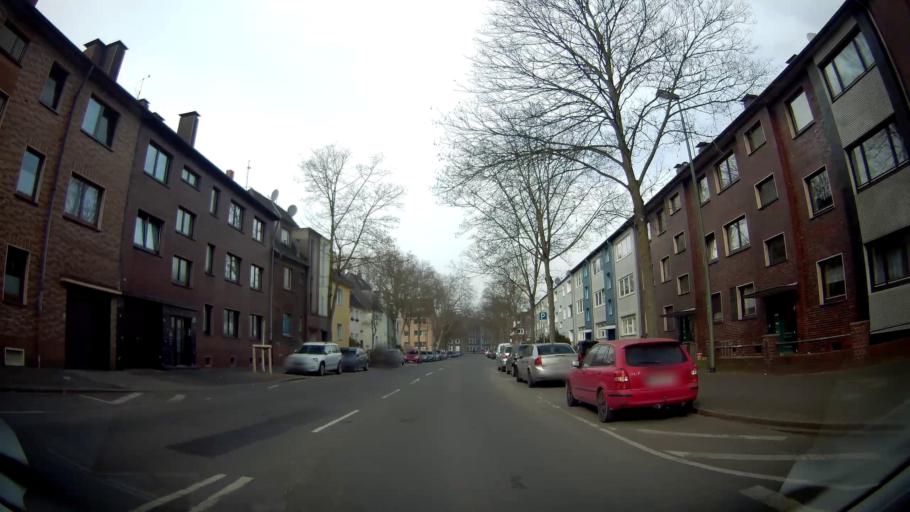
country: DE
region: North Rhine-Westphalia
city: Meiderich
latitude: 51.4854
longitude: 6.7783
